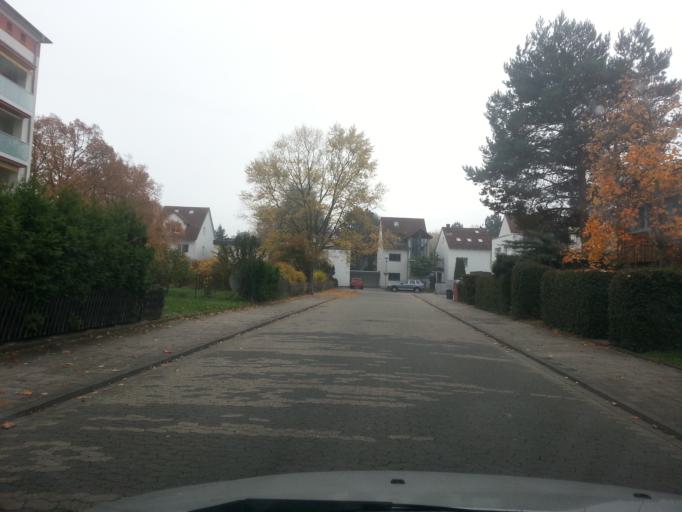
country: DE
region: Hesse
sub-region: Regierungsbezirk Darmstadt
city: Darmstadt
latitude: 49.9018
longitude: 8.6582
